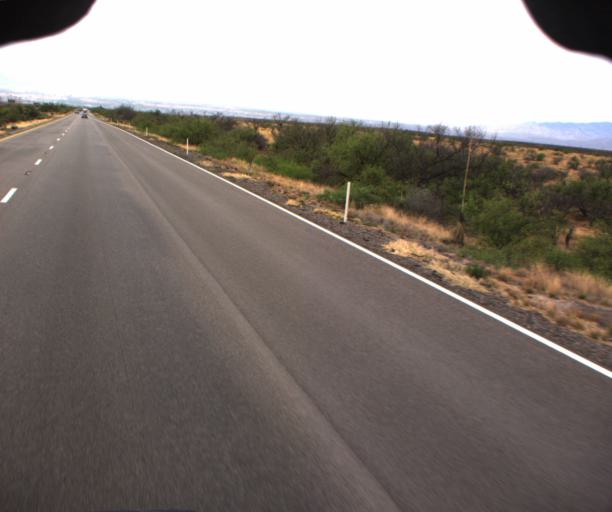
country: US
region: Arizona
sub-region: Cochise County
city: Saint David
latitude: 31.9914
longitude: -110.1800
